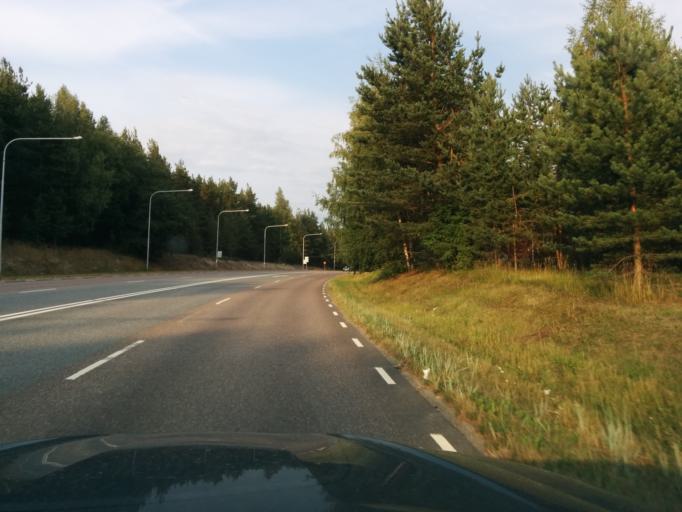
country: SE
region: Vaesternorrland
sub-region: OErnskoeldsviks Kommun
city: Ornskoldsvik
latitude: 63.2747
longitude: 18.6971
